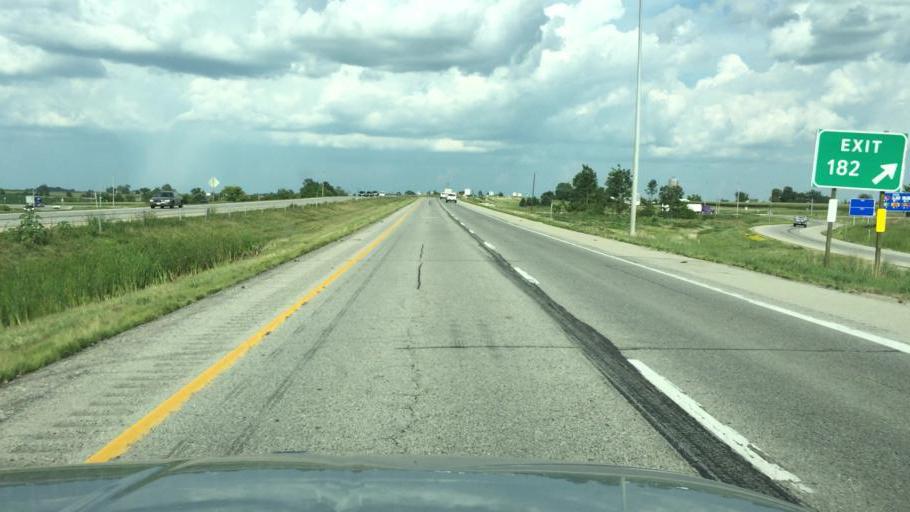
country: US
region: Iowa
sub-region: Poweshiek County
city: Grinnell
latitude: 41.6959
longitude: -92.7318
